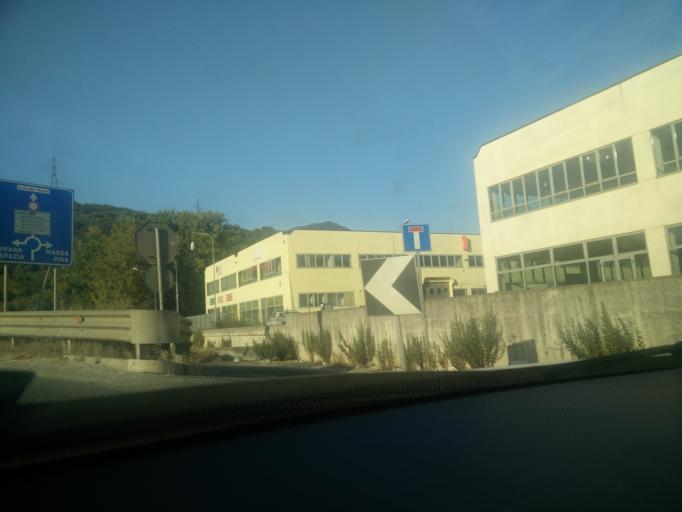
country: IT
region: Tuscany
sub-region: Provincia di Massa-Carrara
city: Carrara
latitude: 44.0421
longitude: 10.0857
